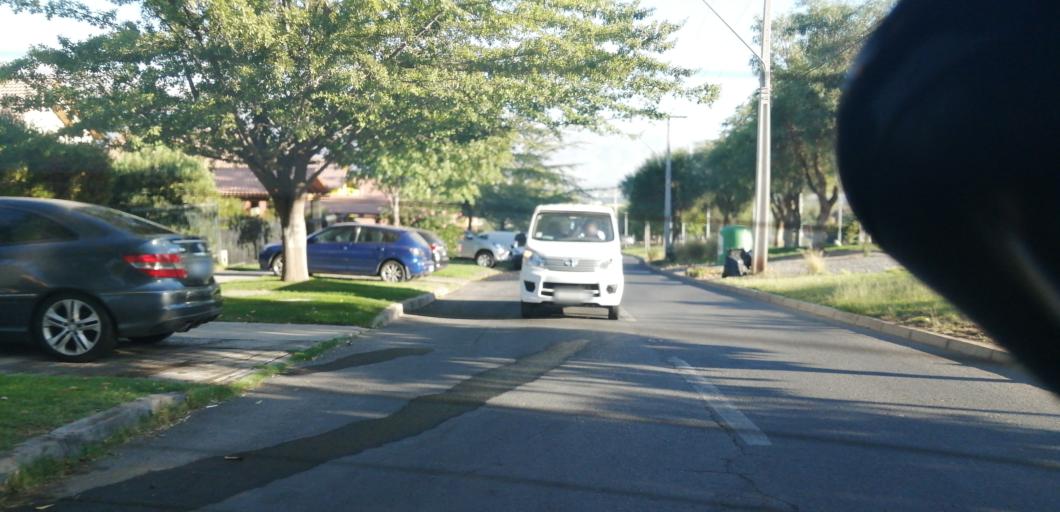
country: CL
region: Santiago Metropolitan
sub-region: Provincia de Santiago
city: Lo Prado
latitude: -33.4564
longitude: -70.8459
